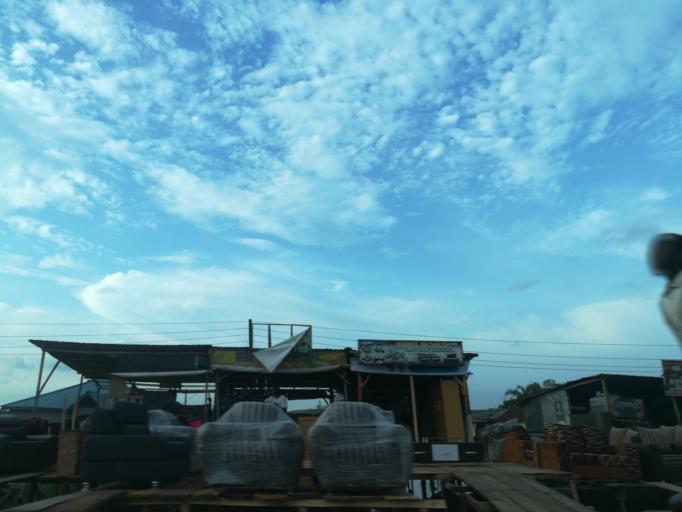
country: NG
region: Lagos
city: Ebute Ikorodu
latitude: 6.6090
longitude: 3.4365
